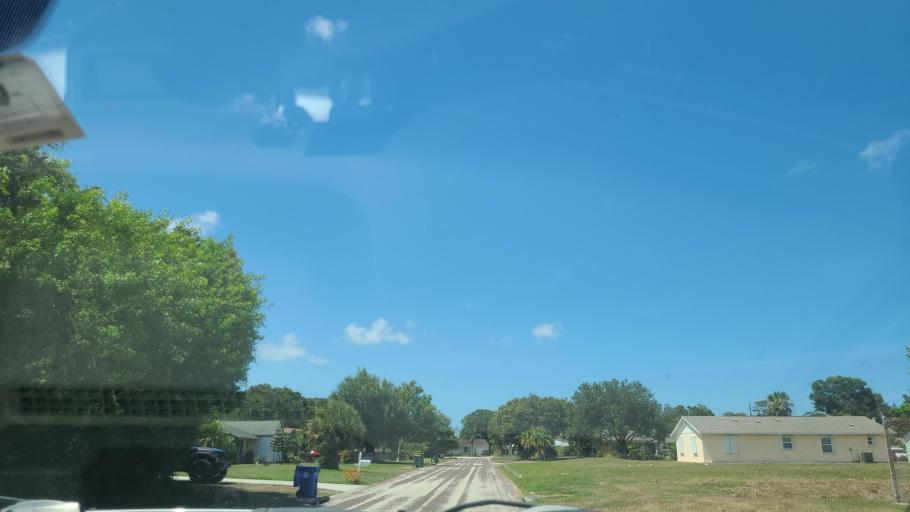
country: US
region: Florida
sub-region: Indian River County
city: Sebastian
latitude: 27.7762
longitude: -80.4694
